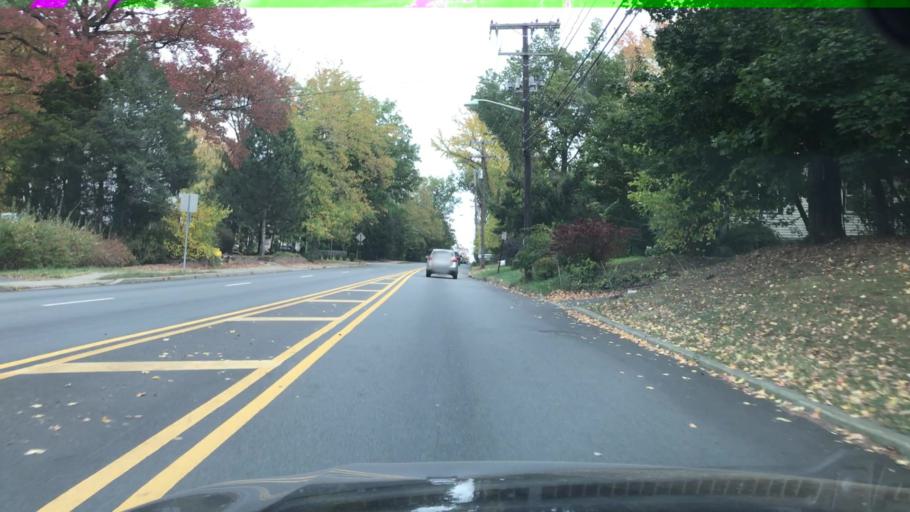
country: US
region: New Jersey
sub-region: Bergen County
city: Teaneck
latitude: 40.9147
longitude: -74.0180
